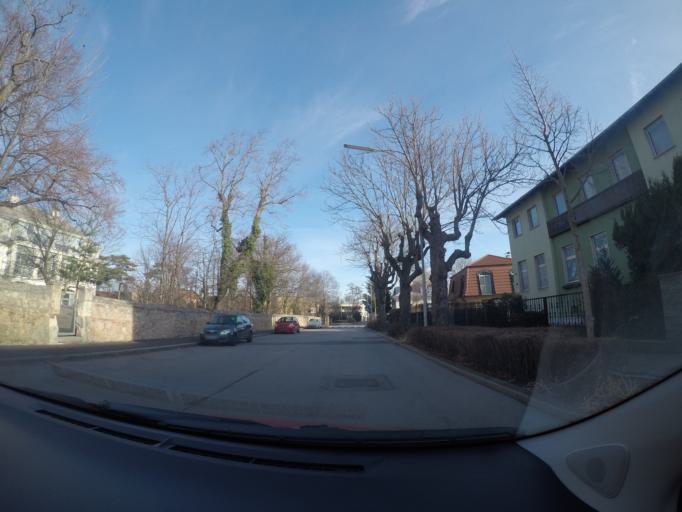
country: AT
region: Lower Austria
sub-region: Politischer Bezirk Baden
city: Baden
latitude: 48.0029
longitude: 16.2345
